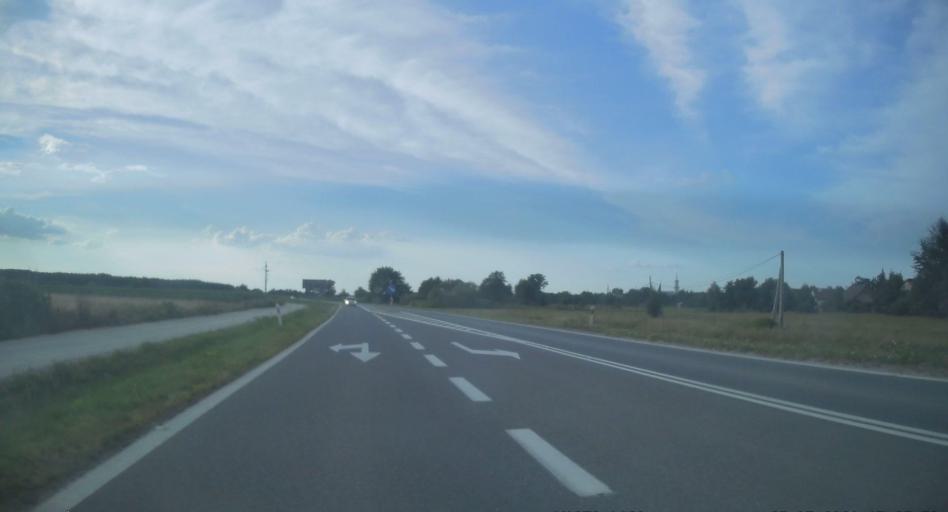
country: PL
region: Lesser Poland Voivodeship
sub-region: Powiat brzeski
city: Szczurowa
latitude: 50.0844
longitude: 20.6318
